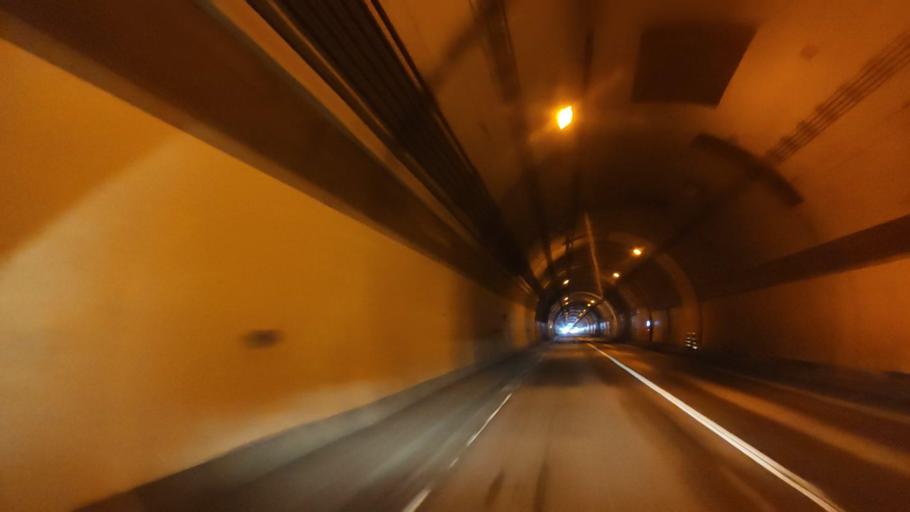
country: JP
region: Hokkaido
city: Rumoi
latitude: 43.8050
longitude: 141.3897
